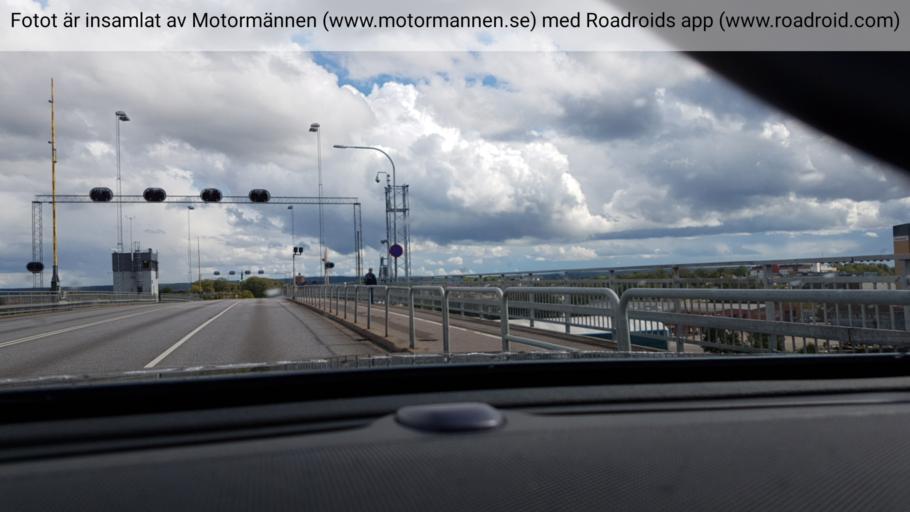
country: SE
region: Vaestra Goetaland
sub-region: Vanersborgs Kommun
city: Vanersborg
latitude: 58.3828
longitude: 12.3089
